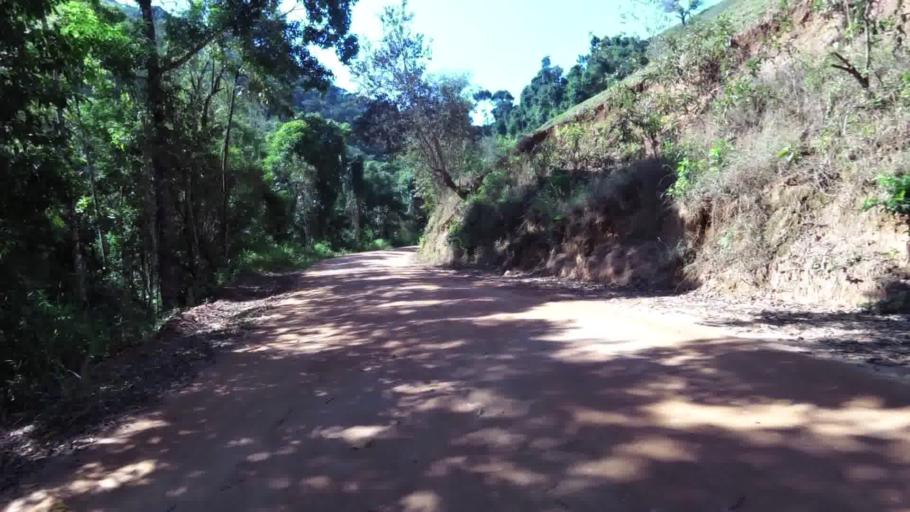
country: BR
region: Espirito Santo
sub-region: Alfredo Chaves
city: Alfredo Chaves
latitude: -20.5742
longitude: -40.7892
